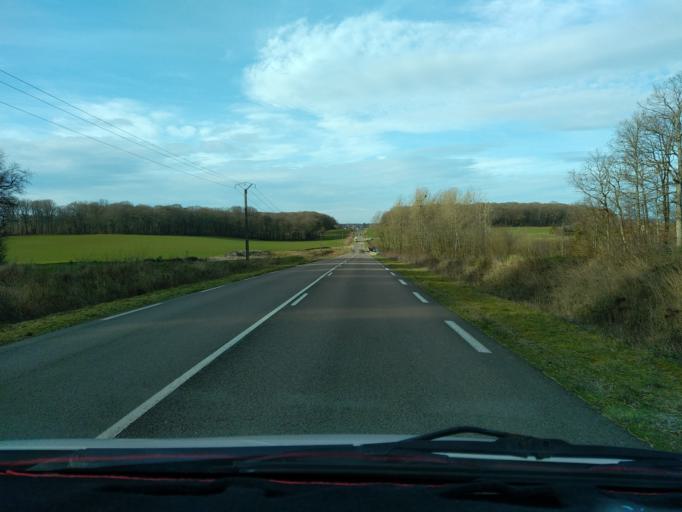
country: FR
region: Franche-Comte
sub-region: Departement de la Haute-Saone
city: Gray
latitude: 47.4171
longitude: 5.6232
